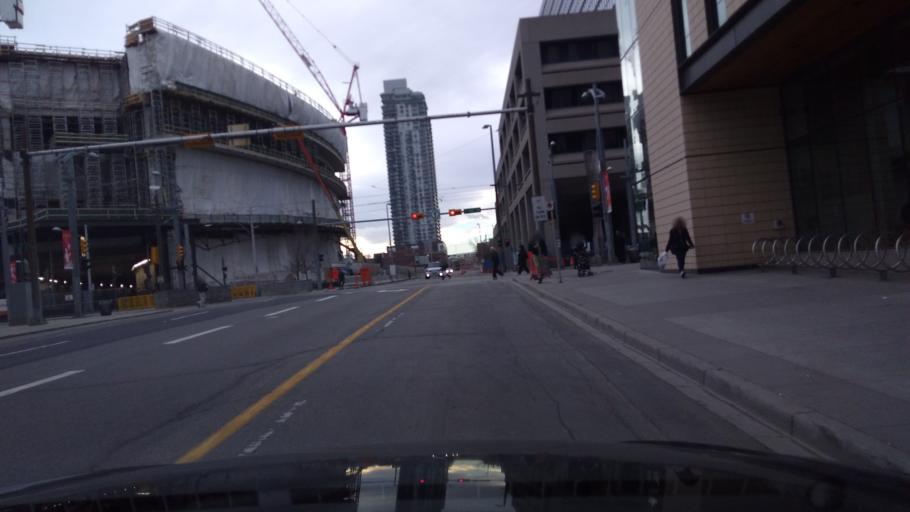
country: CA
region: Alberta
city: Calgary
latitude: 51.0467
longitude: -114.0558
